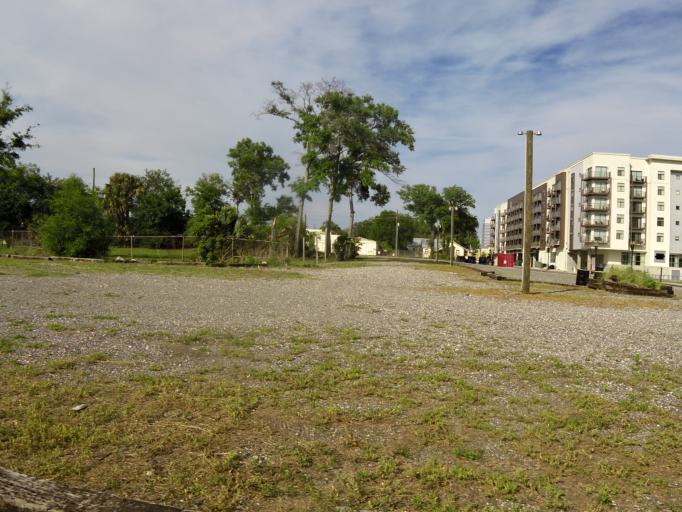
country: US
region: Florida
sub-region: Duval County
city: Jacksonville
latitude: 30.3223
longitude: -81.6754
